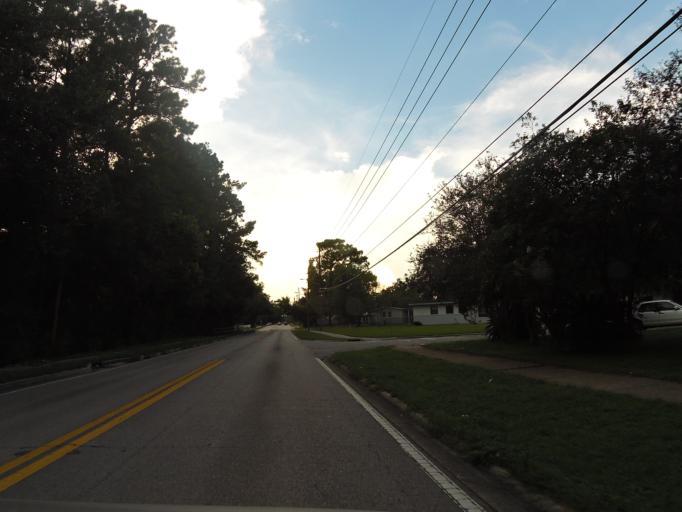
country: US
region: Florida
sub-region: Clay County
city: Bellair-Meadowbrook Terrace
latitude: 30.2724
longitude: -81.7813
